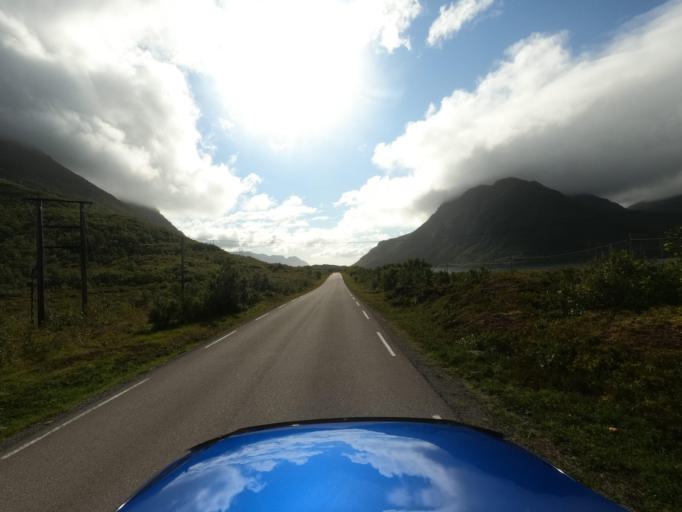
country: NO
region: Nordland
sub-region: Vagan
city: Kabelvag
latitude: 68.2813
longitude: 14.1598
